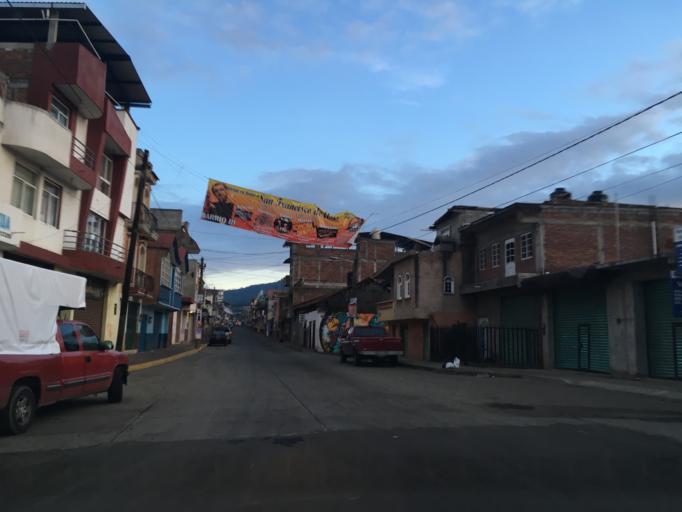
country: MX
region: Michoacan
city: Cheran
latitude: 19.6838
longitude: -101.9552
